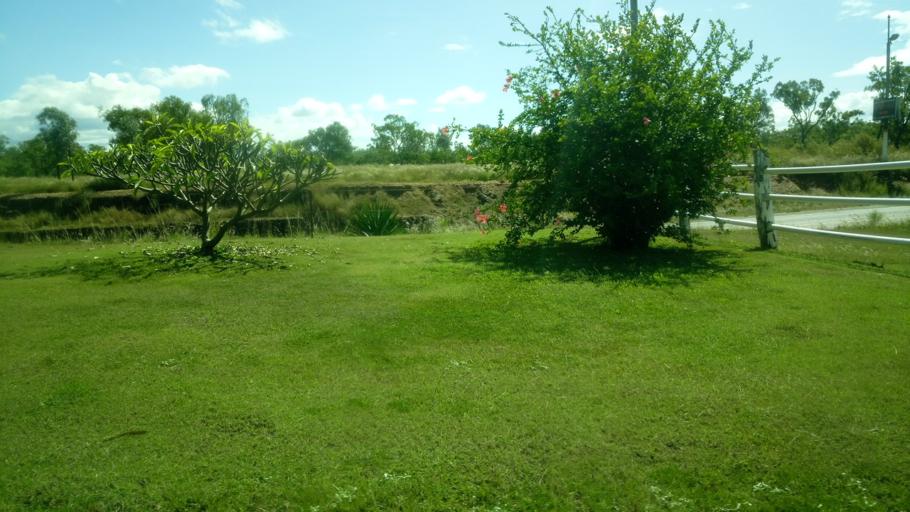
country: AU
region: Queensland
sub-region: Cairns
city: Port Douglas
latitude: -16.1066
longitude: 144.7766
